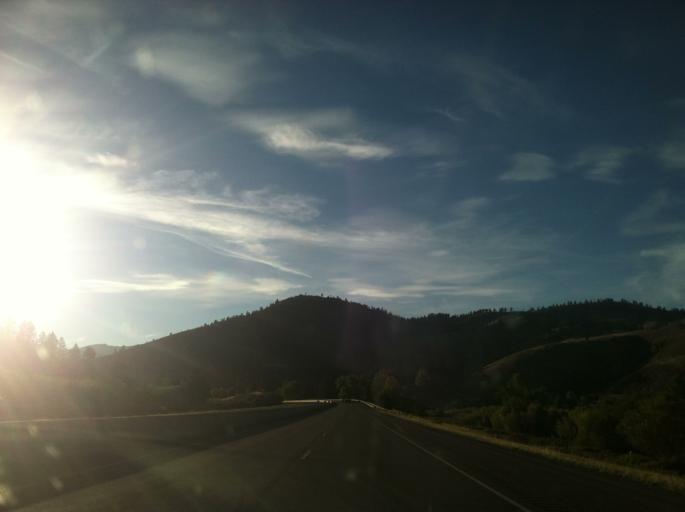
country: US
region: Montana
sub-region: Granite County
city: Philipsburg
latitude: 46.7174
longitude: -113.2902
